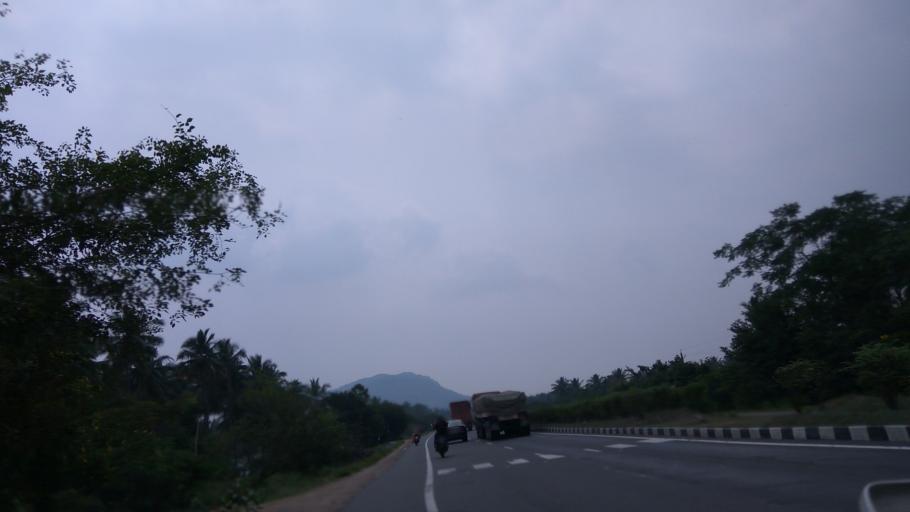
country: IN
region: Tamil Nadu
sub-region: Krishnagiri
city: Kaverippattanam
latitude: 12.3948
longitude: 78.2185
